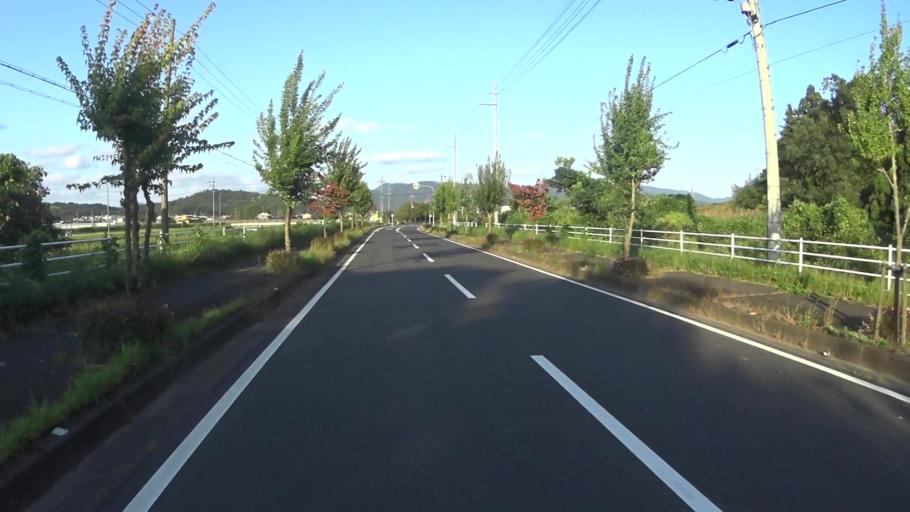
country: JP
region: Kyoto
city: Miyazu
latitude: 35.6050
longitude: 135.0530
